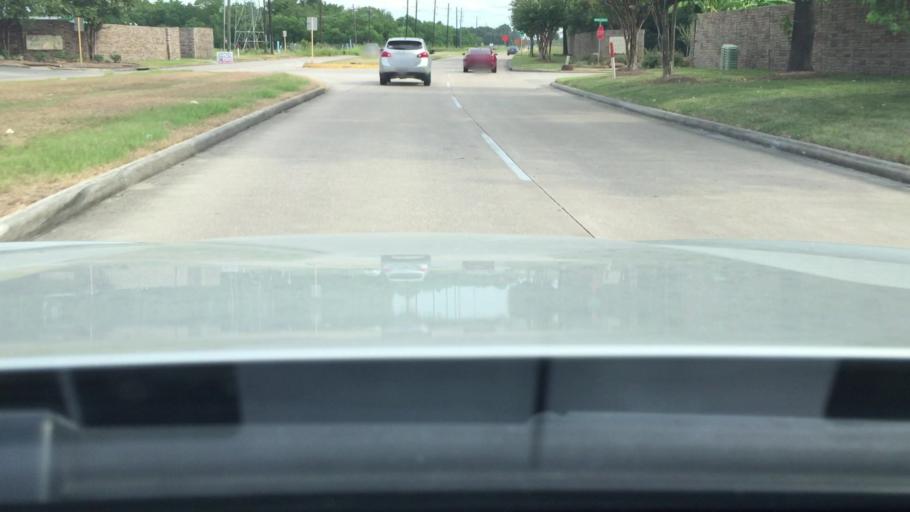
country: US
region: Texas
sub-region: Harris County
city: Jersey Village
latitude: 29.9367
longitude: -95.5466
